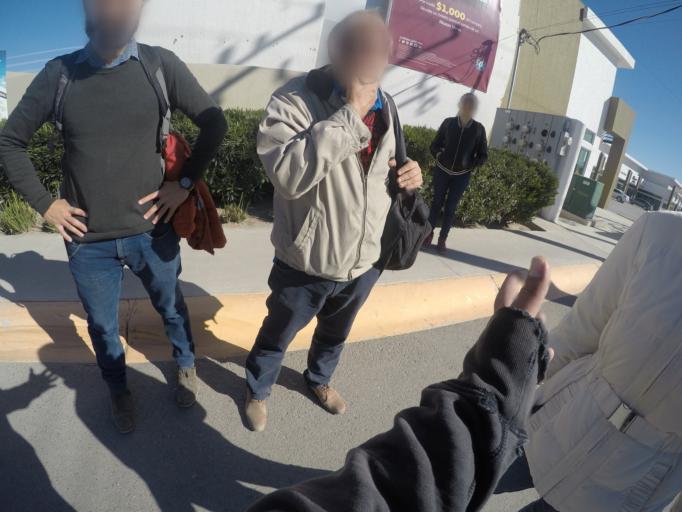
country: US
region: Texas
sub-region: El Paso County
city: Socorro
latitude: 31.6941
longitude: -106.3739
